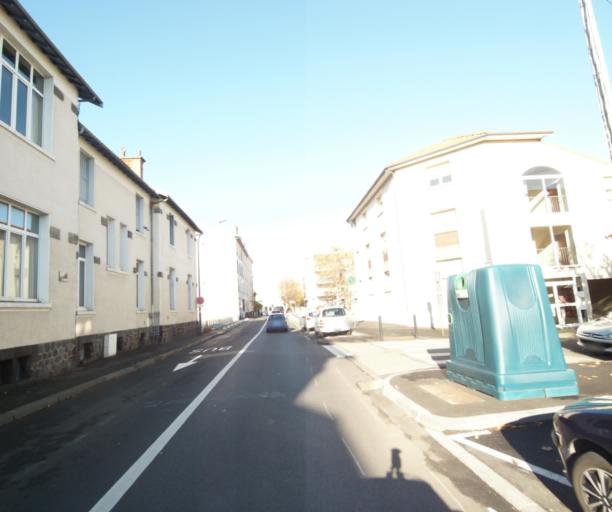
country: FR
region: Auvergne
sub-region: Departement du Puy-de-Dome
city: Clermont-Ferrand
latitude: 45.7740
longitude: 3.0971
